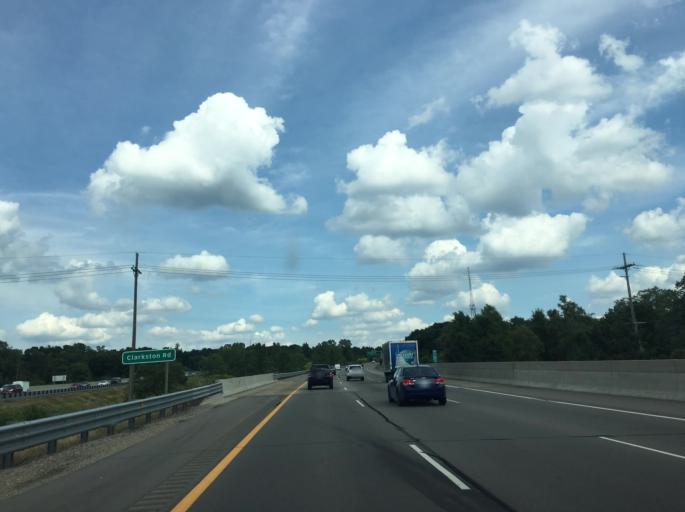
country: US
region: Michigan
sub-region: Oakland County
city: Clarkston
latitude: 42.7454
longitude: -83.4005
